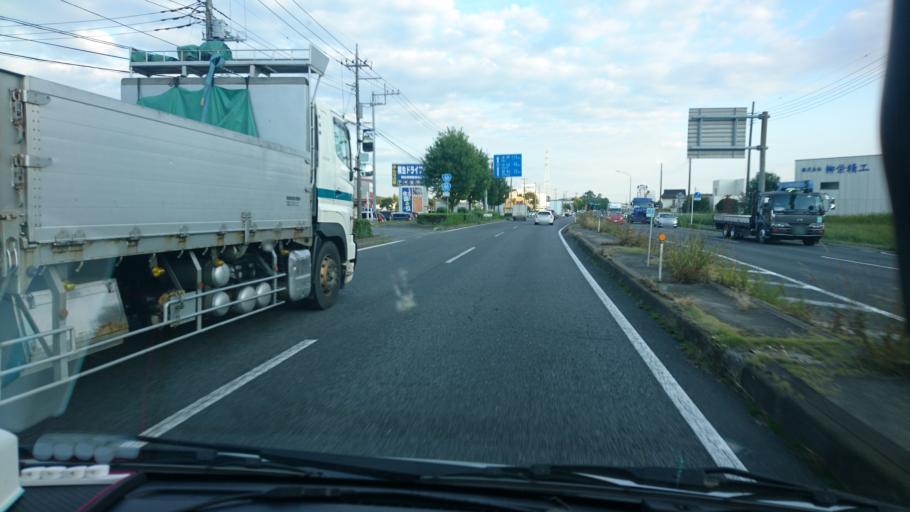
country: JP
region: Gunma
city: Kiryu
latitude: 36.3669
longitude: 139.3623
